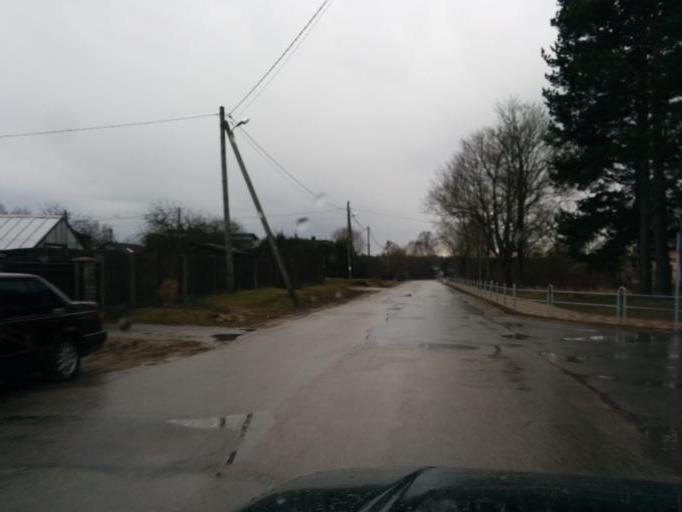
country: LV
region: Kekava
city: Kekava
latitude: 56.8684
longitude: 24.1836
